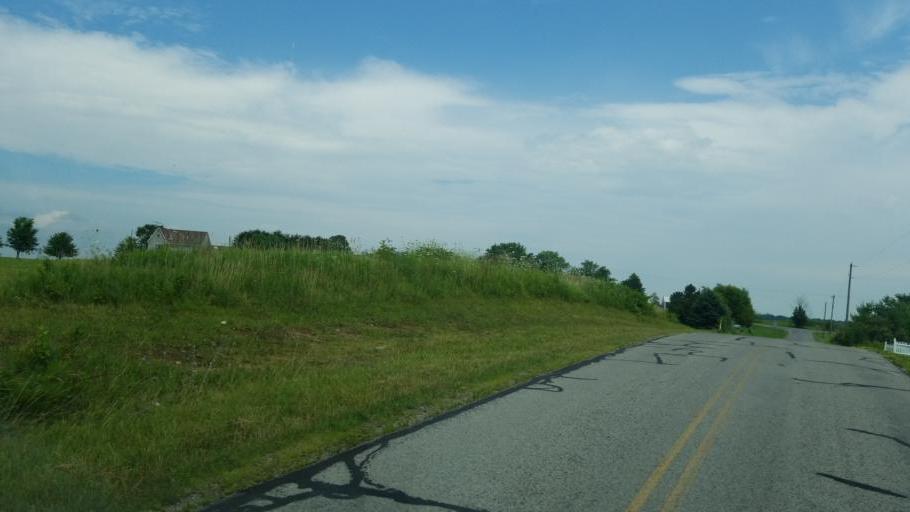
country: US
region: Ohio
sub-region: Logan County
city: Northwood
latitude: 40.4147
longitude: -83.6654
